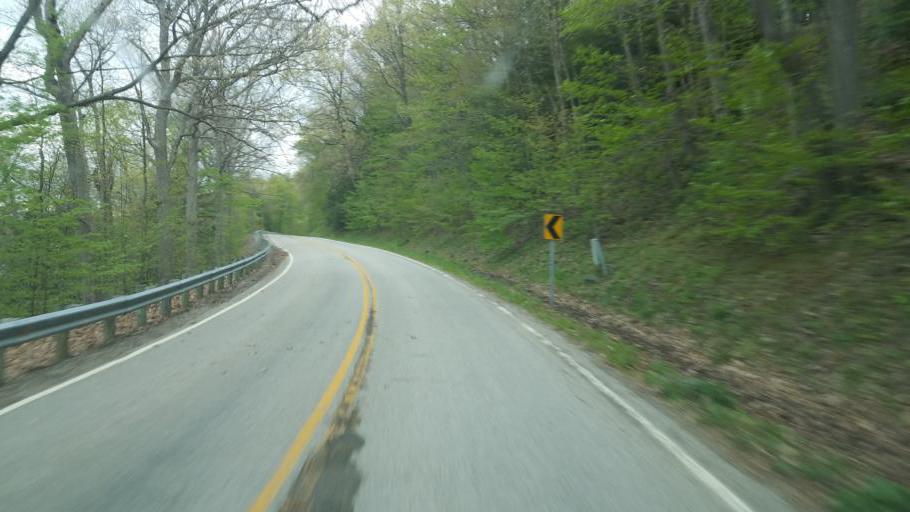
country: US
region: Ohio
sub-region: Ashland County
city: Loudonville
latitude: 40.6382
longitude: -82.3246
